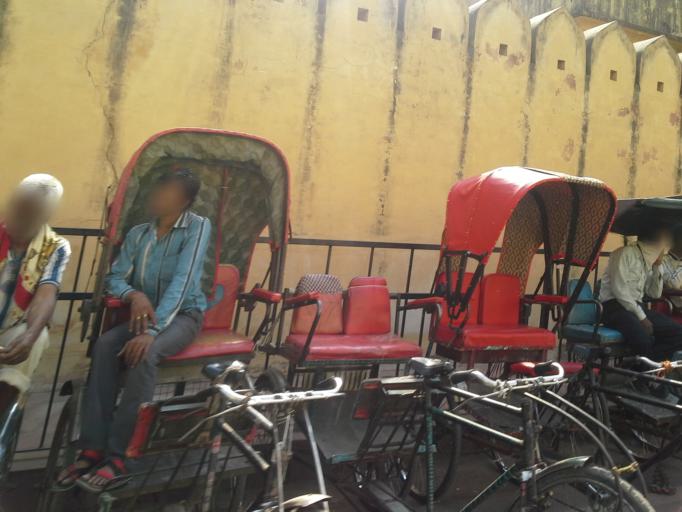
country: IN
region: Rajasthan
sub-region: Jaipur
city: Jaipur
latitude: 26.9252
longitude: 75.8239
